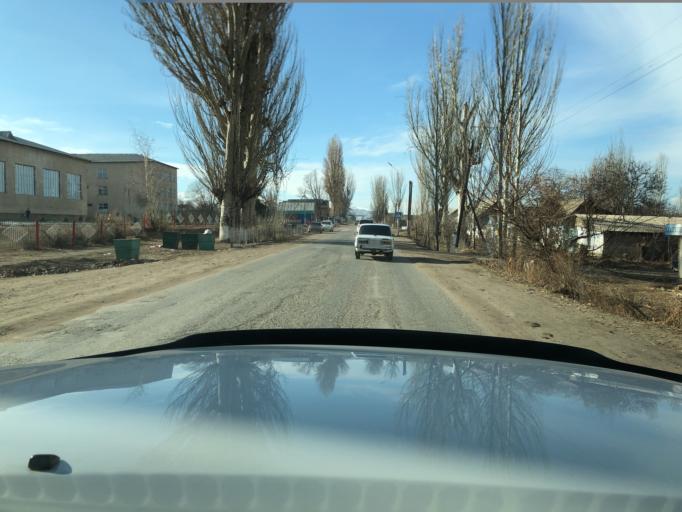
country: KG
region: Ysyk-Koel
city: Pokrovka
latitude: 42.3360
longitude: 77.9914
